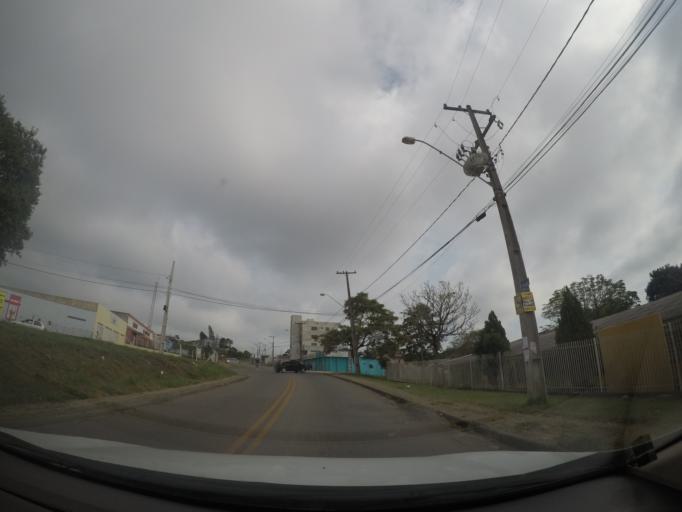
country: BR
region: Parana
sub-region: Colombo
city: Colombo
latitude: -25.3485
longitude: -49.2155
